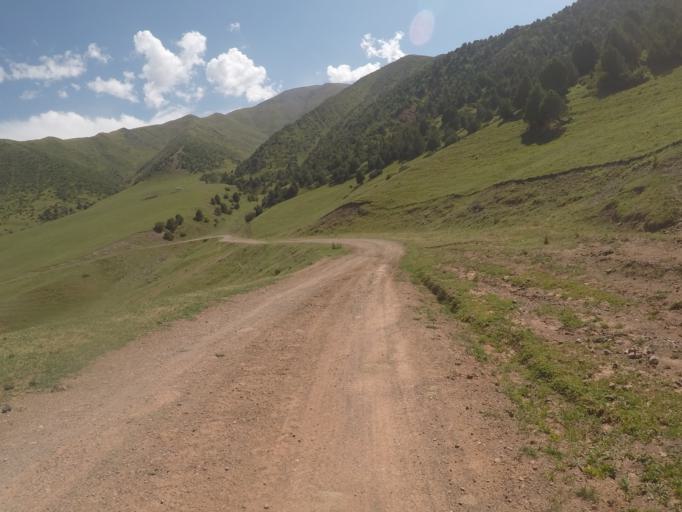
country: KG
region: Chuy
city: Bishkek
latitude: 42.6451
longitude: 74.5700
